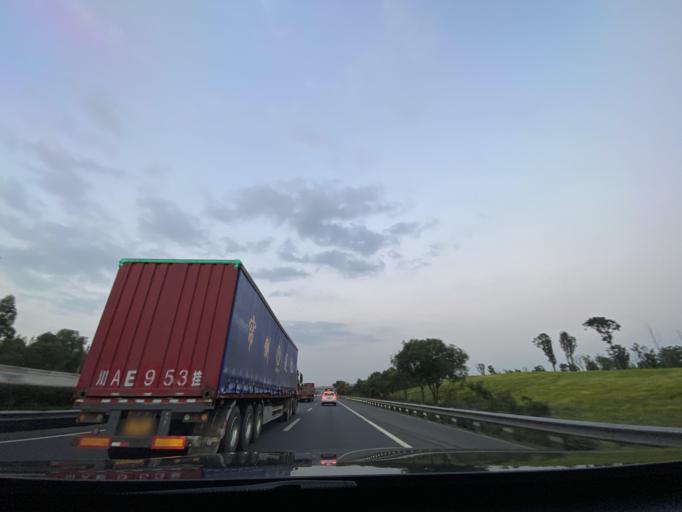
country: CN
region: Sichuan
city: Chengdu
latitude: 30.5712
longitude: 104.1251
